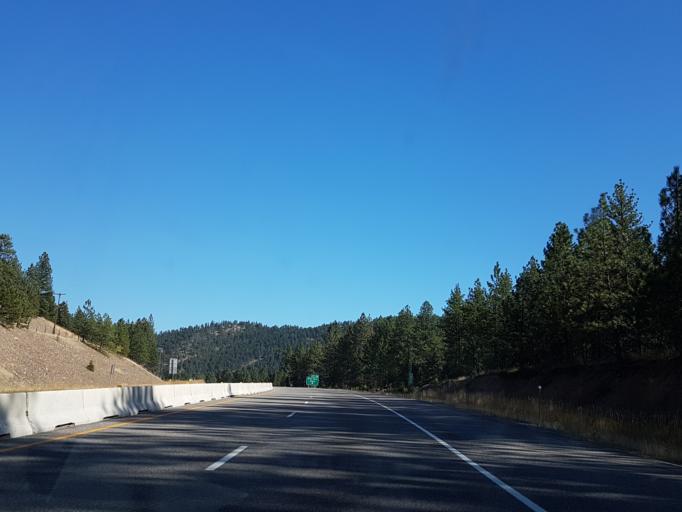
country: US
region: Montana
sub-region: Missoula County
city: Frenchtown
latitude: 47.0195
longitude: -114.3763
